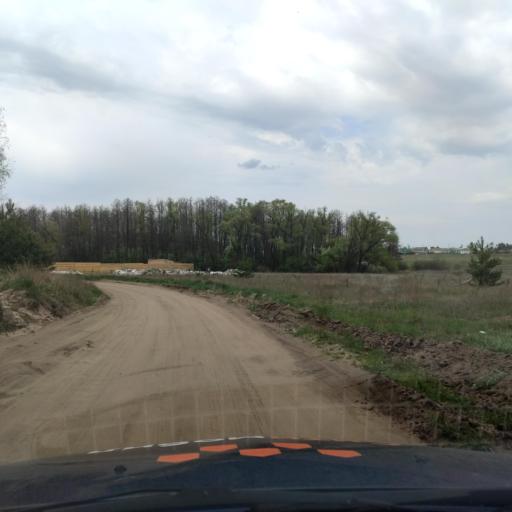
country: RU
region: Voronezj
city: Podgornoye
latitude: 51.8677
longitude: 39.1709
